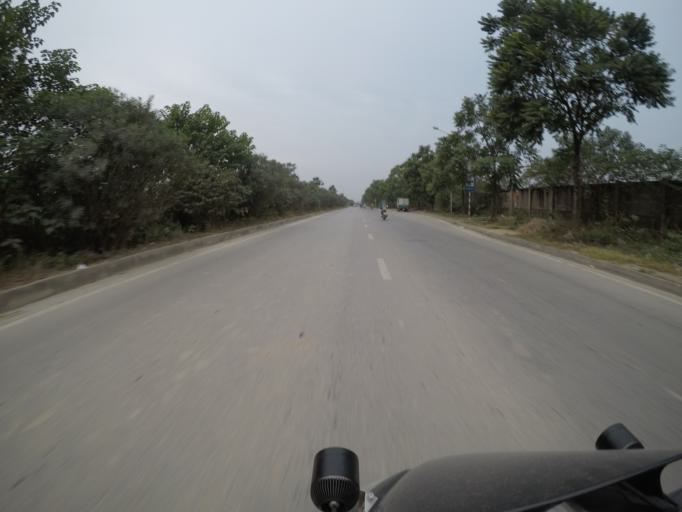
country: VN
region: Ha Noi
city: Cau Dien
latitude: 21.0085
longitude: 105.7553
